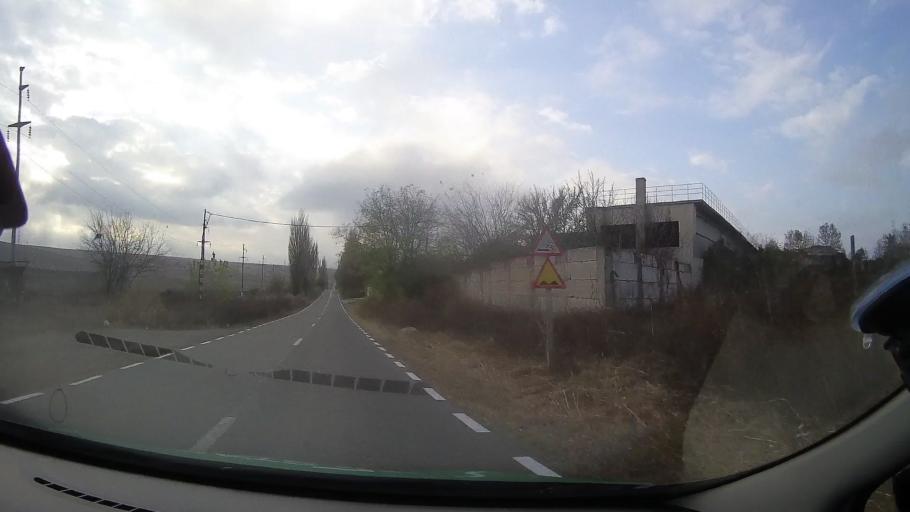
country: RO
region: Constanta
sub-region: Comuna Mircea Voda
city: Satu Nou
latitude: 44.2359
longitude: 28.2335
